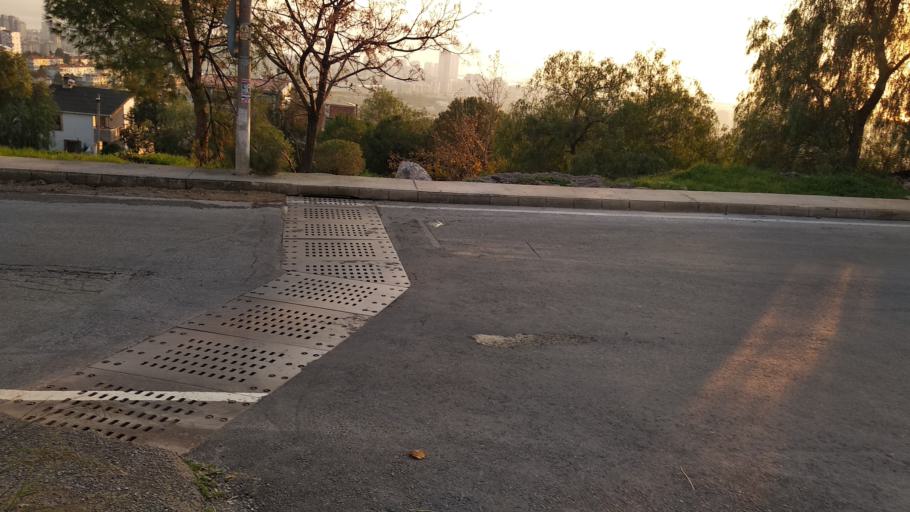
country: TR
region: Izmir
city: Karsiyaka
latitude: 38.4968
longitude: 27.0808
